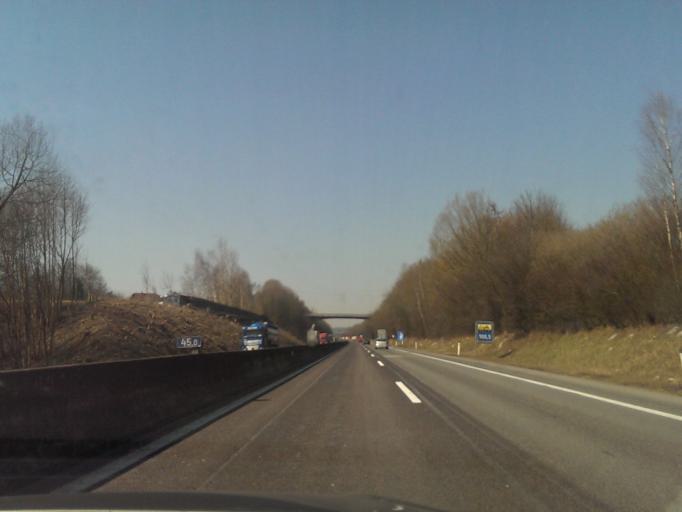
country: AT
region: Upper Austria
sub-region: Politischer Bezirk Vocklabruck
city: Wolfsegg am Hausruck
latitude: 48.2166
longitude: 13.6222
